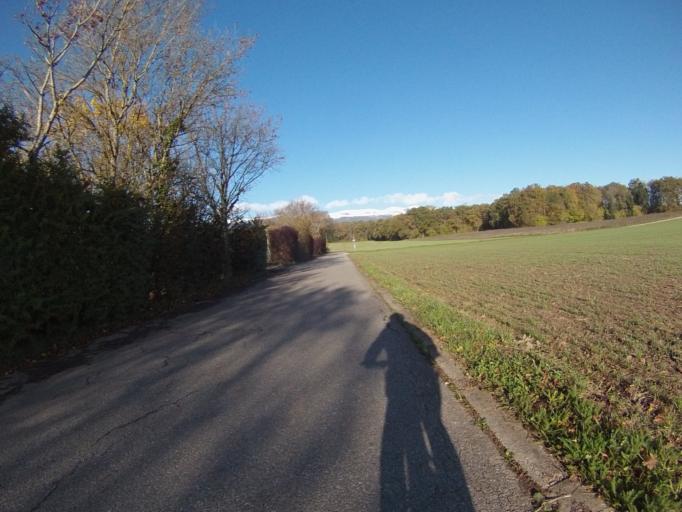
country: CH
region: Geneva
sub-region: Geneva
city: Meyrin
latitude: 46.2393
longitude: 6.0716
